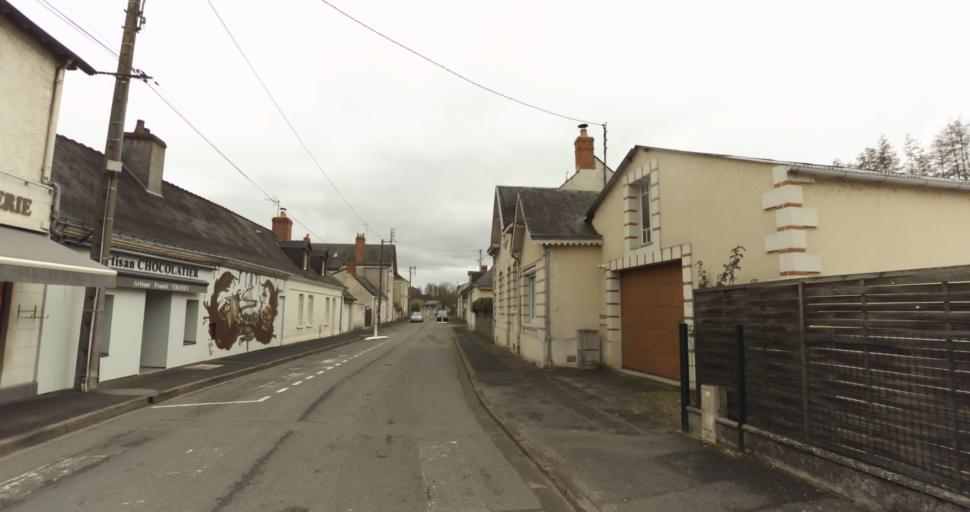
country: FR
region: Pays de la Loire
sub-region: Departement de Maine-et-Loire
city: Jumelles
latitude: 47.3853
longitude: -0.1141
